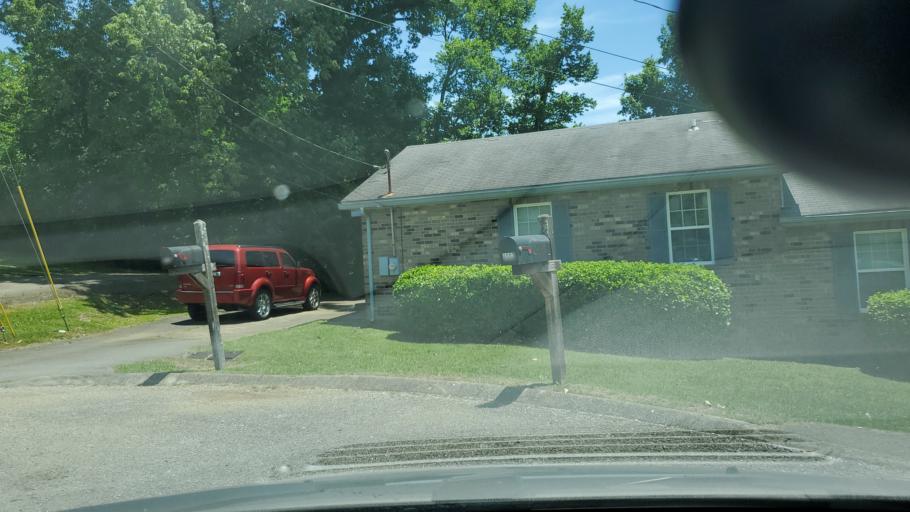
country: US
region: Tennessee
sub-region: Davidson County
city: Nashville
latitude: 36.2218
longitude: -86.7529
